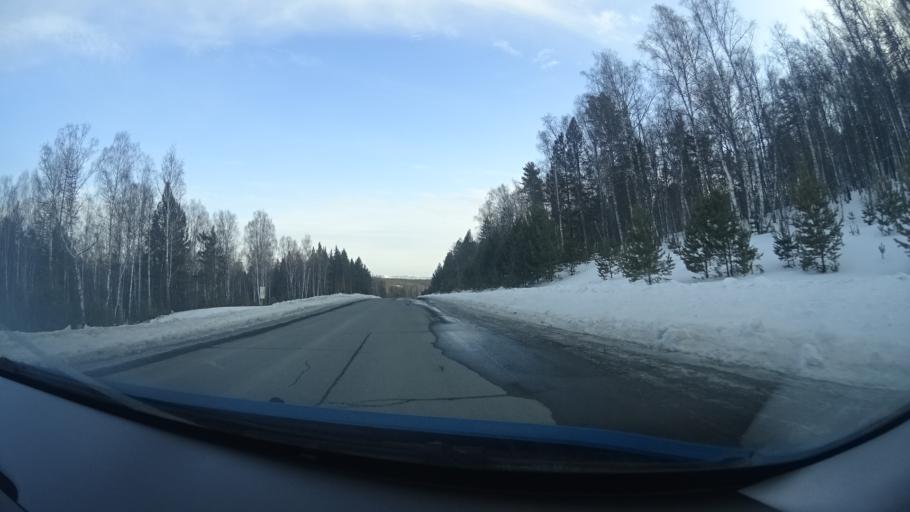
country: RU
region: Bashkortostan
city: Lomovka
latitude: 53.4802
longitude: 58.3149
